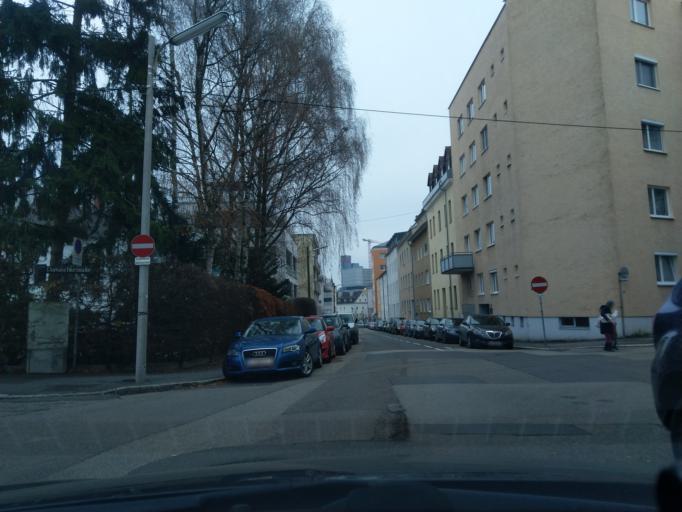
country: AT
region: Upper Austria
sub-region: Linz Stadt
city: Linz
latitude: 48.3154
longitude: 14.2777
